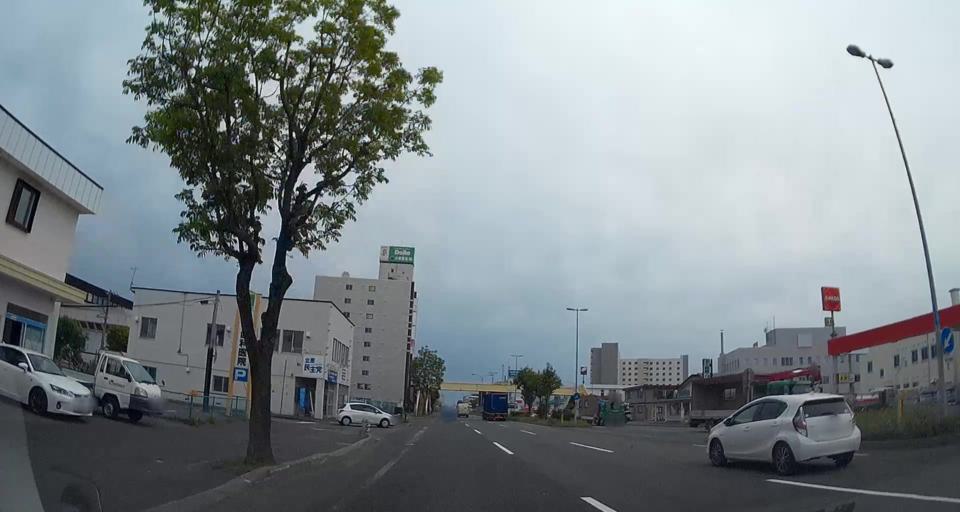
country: JP
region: Hokkaido
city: Tomakomai
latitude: 42.6373
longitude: 141.6089
